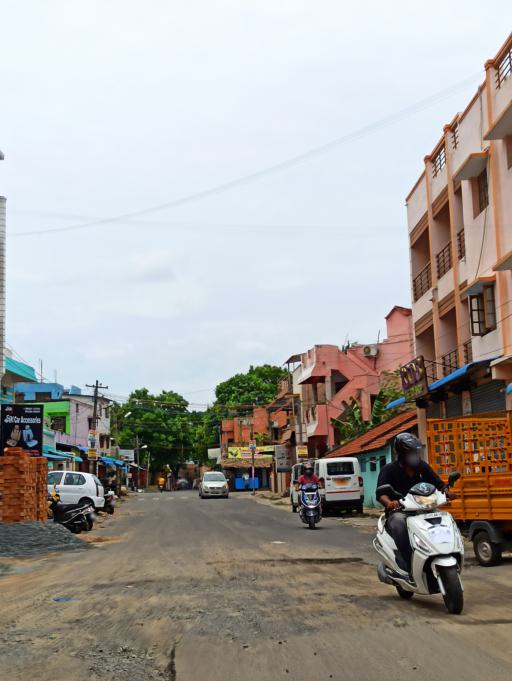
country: IN
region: Tamil Nadu
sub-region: Kancheepuram
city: Vandalur
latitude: 12.9263
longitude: 80.1073
